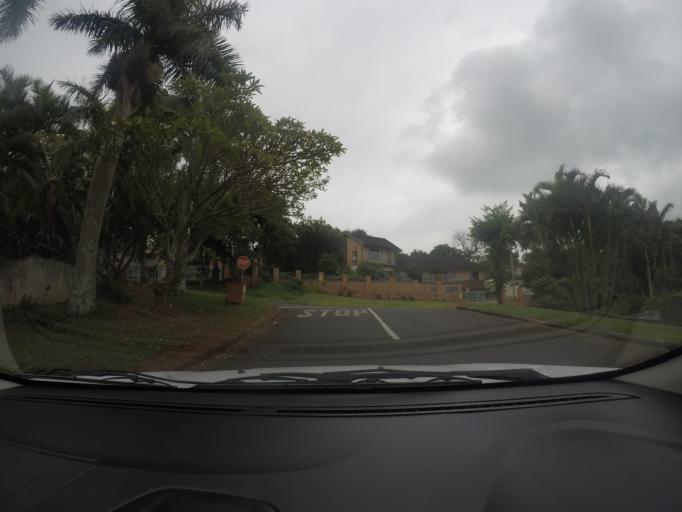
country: ZA
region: KwaZulu-Natal
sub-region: uThungulu District Municipality
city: Empangeni
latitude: -28.7566
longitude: 31.8880
